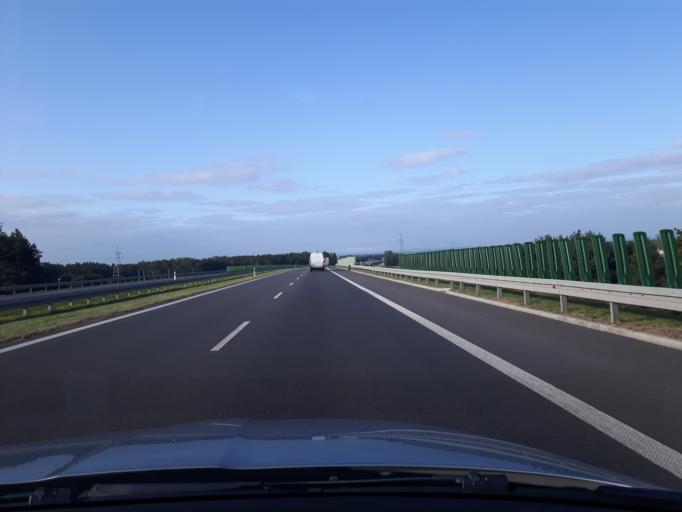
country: PL
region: Masovian Voivodeship
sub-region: Powiat szydlowiecki
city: Oronsko
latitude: 51.2909
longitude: 20.9821
